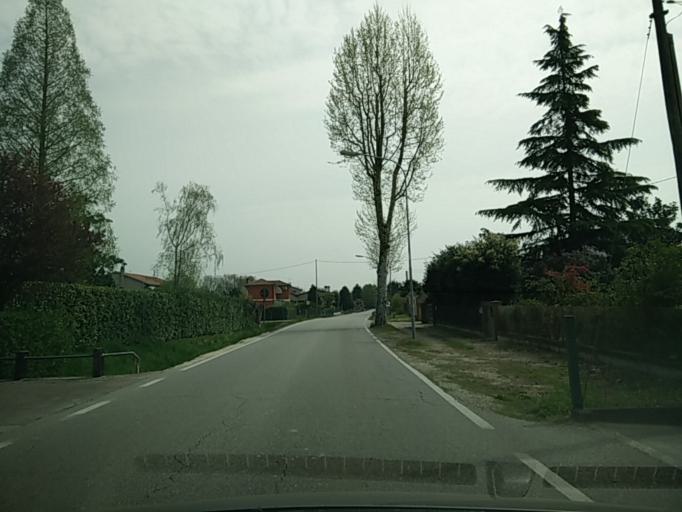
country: IT
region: Veneto
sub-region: Provincia di Venezia
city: Scaltenigo
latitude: 45.4729
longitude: 12.0638
